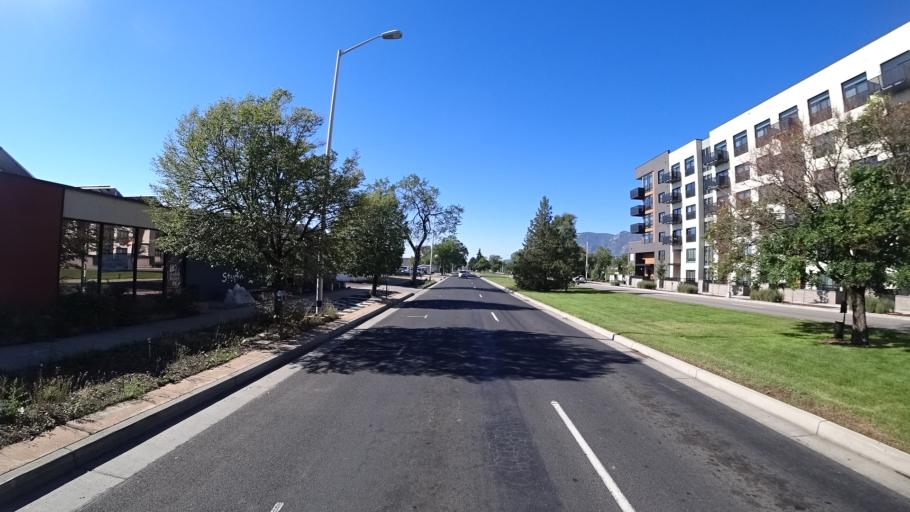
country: US
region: Colorado
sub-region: El Paso County
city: Colorado Springs
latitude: 38.8322
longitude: -104.8180
